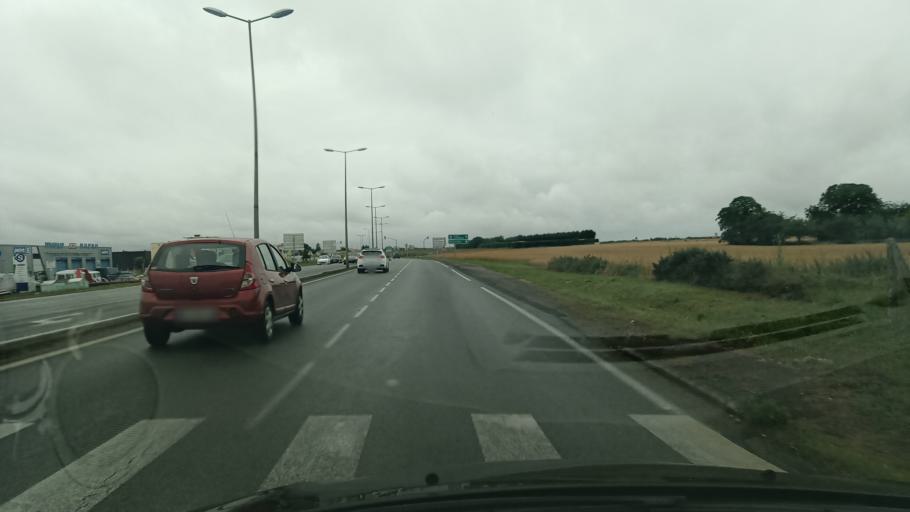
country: FR
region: Poitou-Charentes
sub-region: Departement de la Vienne
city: Poitiers
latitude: 46.6015
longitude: 0.3241
